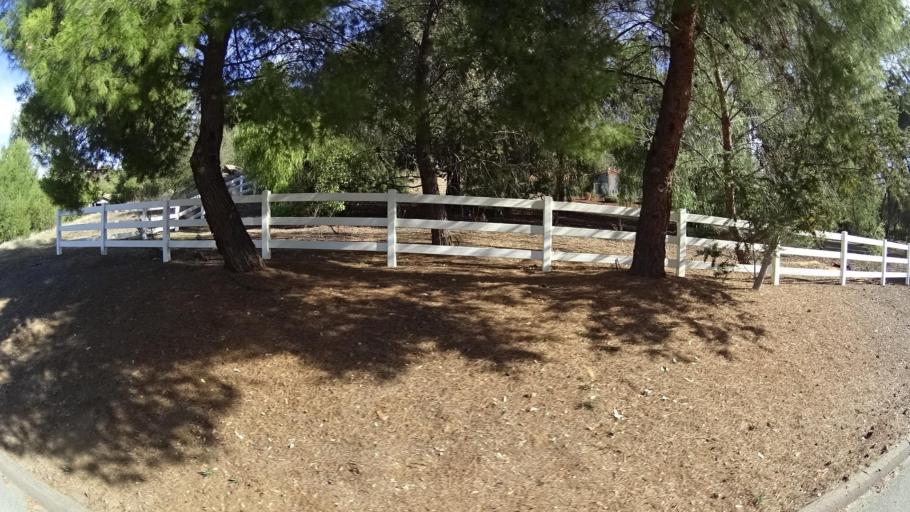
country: US
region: California
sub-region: San Diego County
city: Alpine
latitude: 32.8148
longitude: -116.7377
